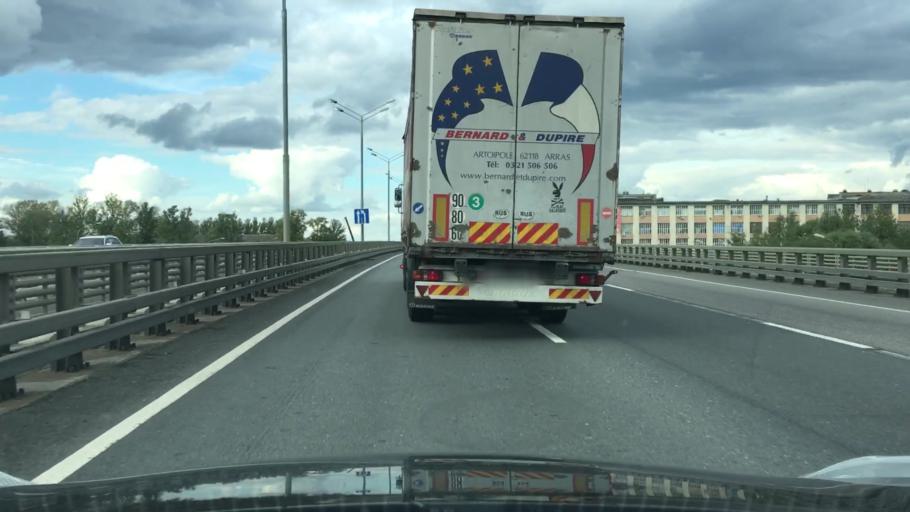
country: RU
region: Tverskaya
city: Tver
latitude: 56.8419
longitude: 35.7919
